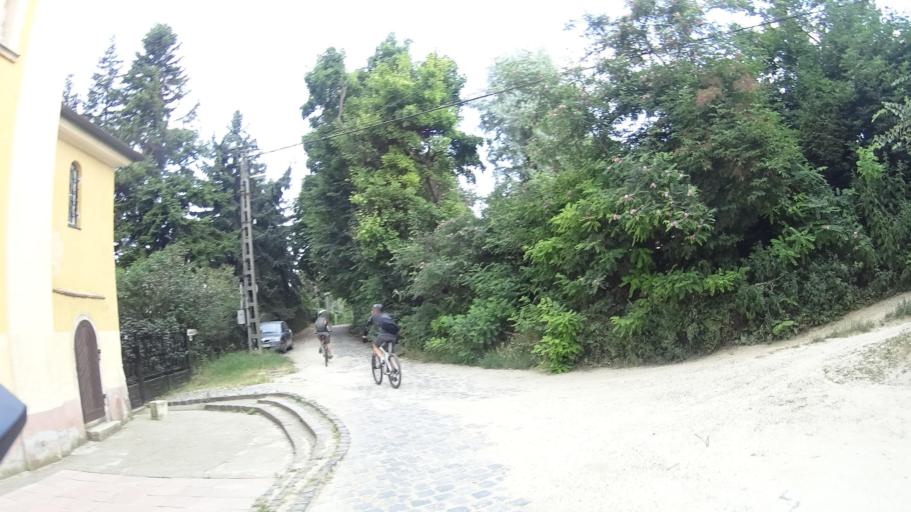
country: HU
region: Pest
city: Budakeszi
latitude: 47.4982
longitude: 18.9446
